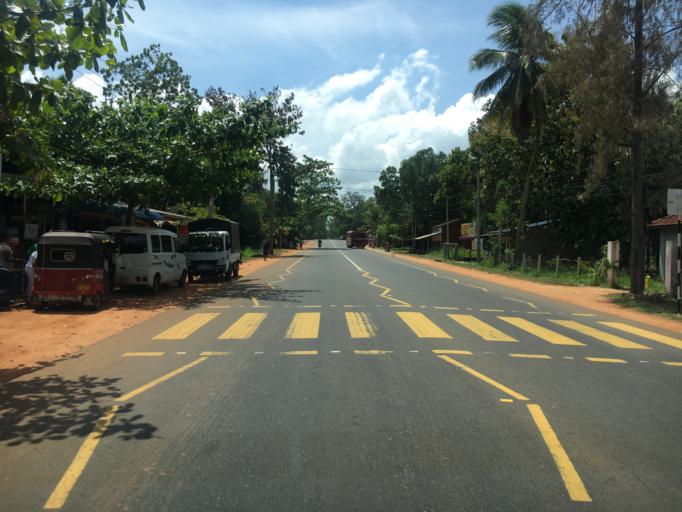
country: LK
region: North Central
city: Anuradhapura
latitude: 8.2710
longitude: 80.5014
